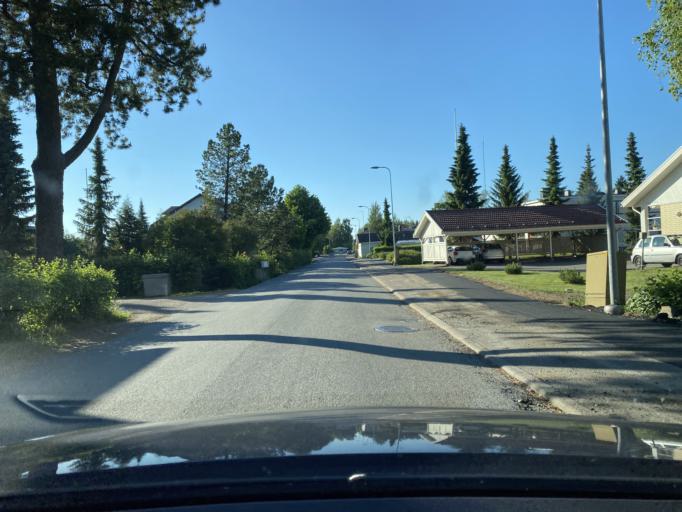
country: FI
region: Satakunta
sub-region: Pori
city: Huittinen
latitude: 61.1728
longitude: 22.6956
